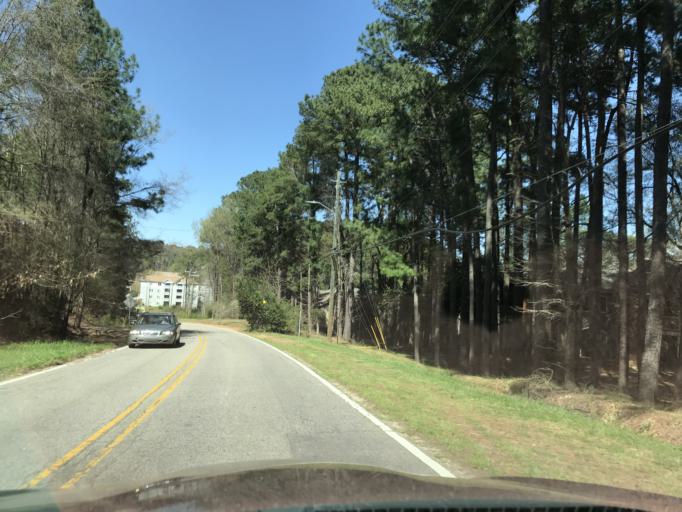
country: US
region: North Carolina
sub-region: Wake County
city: West Raleigh
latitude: 35.7599
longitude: -78.7039
